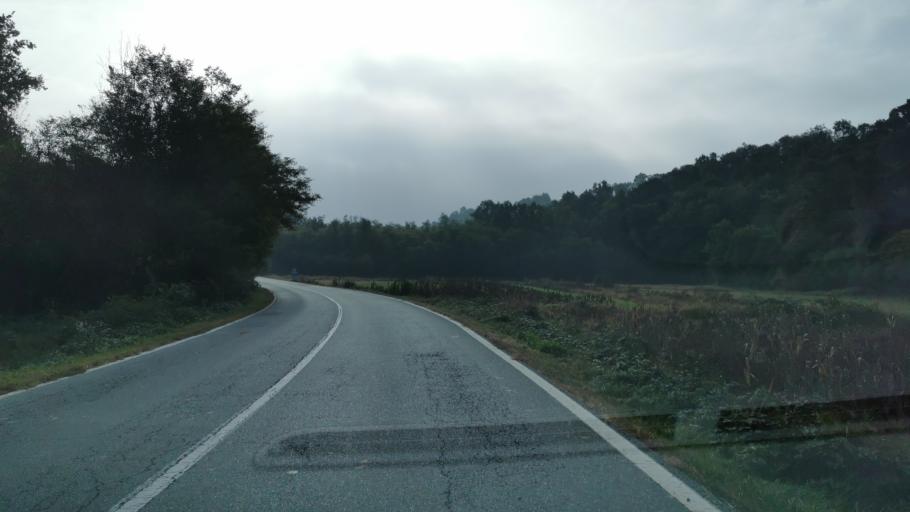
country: IT
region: Piedmont
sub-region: Provincia di Torino
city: Front
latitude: 45.2690
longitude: 7.6829
